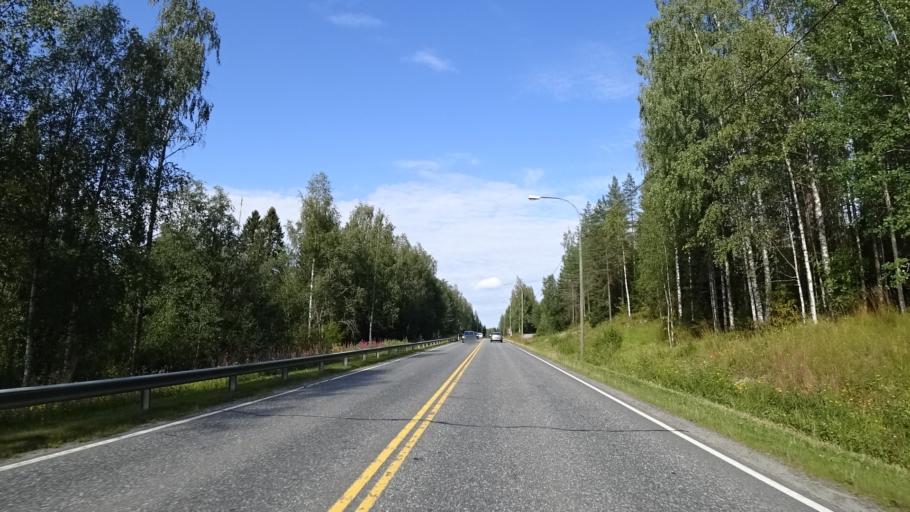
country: FI
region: North Karelia
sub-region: Joensuu
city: Eno
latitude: 62.7862
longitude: 30.0794
